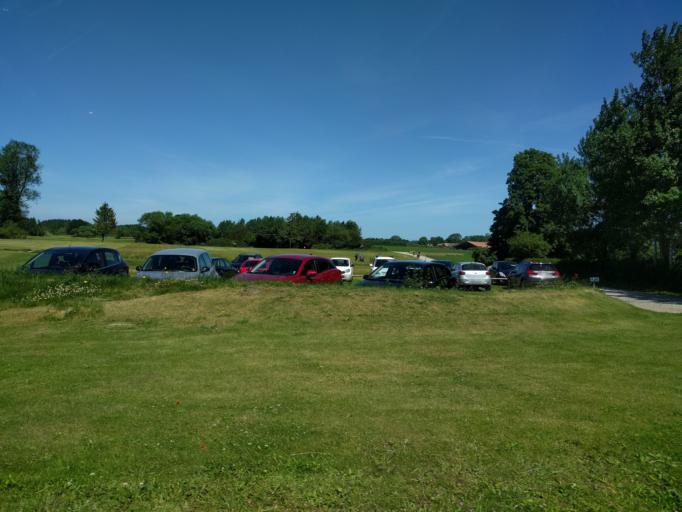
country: DK
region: South Denmark
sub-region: Kerteminde Kommune
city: Langeskov
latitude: 55.3418
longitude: 10.5982
